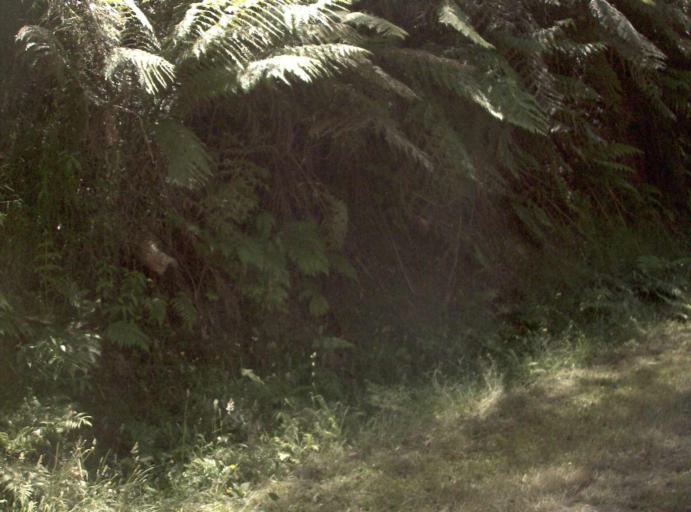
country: AU
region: Victoria
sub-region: Yarra Ranges
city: Millgrove
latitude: -37.7193
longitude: 145.7169
